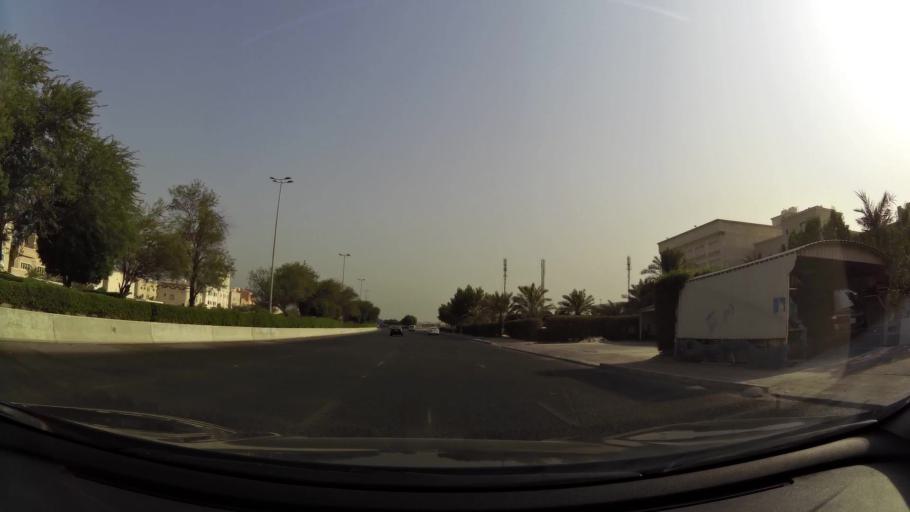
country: KW
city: Al Funaytis
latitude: 29.2310
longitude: 48.0745
